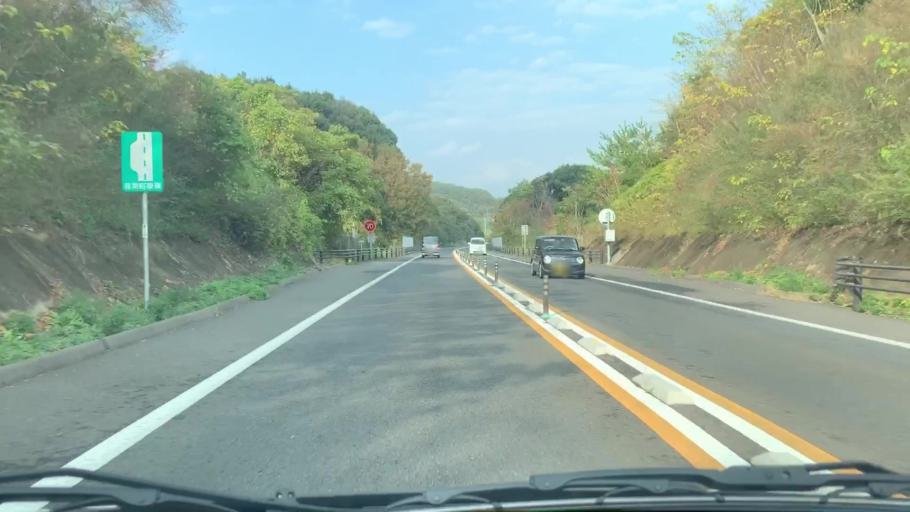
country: JP
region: Nagasaki
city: Sasebo
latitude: 33.0156
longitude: 129.7310
